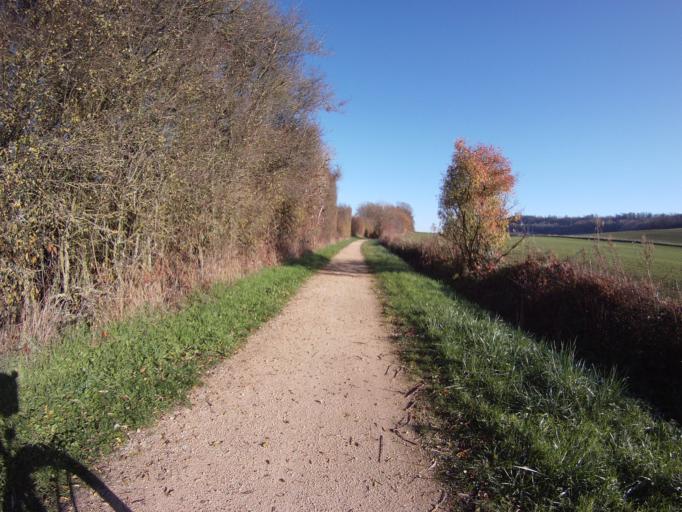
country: FR
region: Lorraine
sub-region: Departement de Meurthe-et-Moselle
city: Bouxieres-aux-Chenes
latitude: 48.7962
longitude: 6.2388
